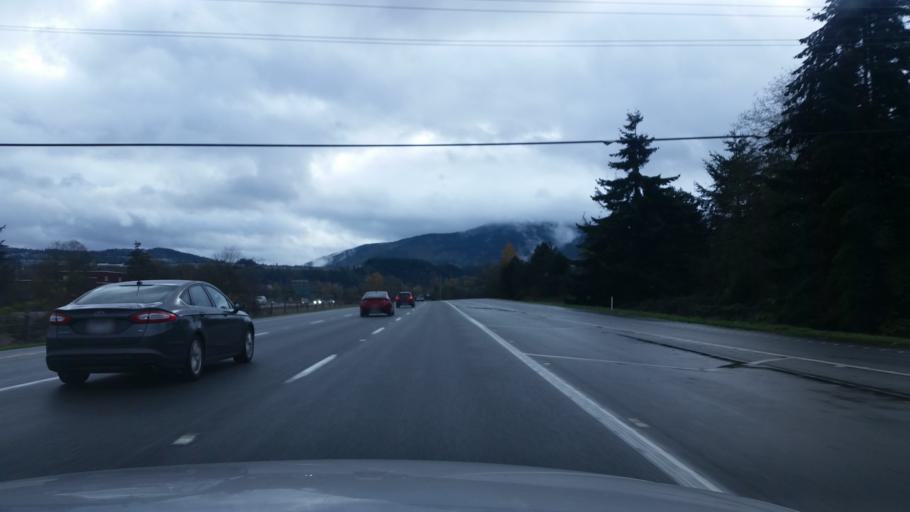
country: US
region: Washington
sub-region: King County
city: Issaquah
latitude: 47.5470
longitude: -122.0577
